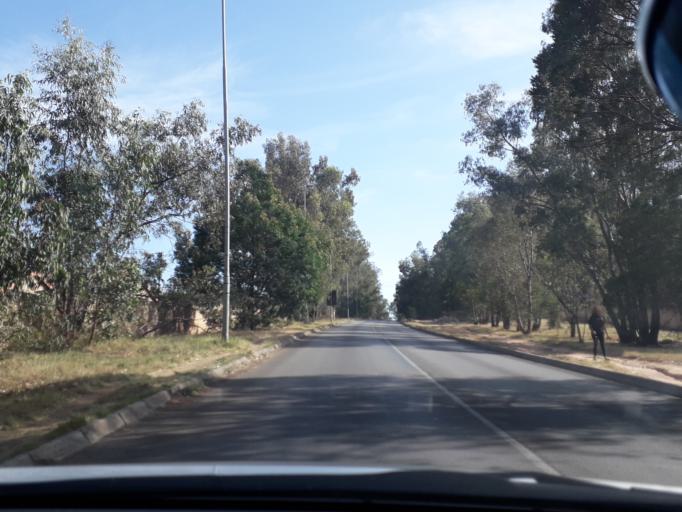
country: ZA
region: Gauteng
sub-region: City of Johannesburg Metropolitan Municipality
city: Roodepoort
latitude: -26.1105
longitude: 27.8969
